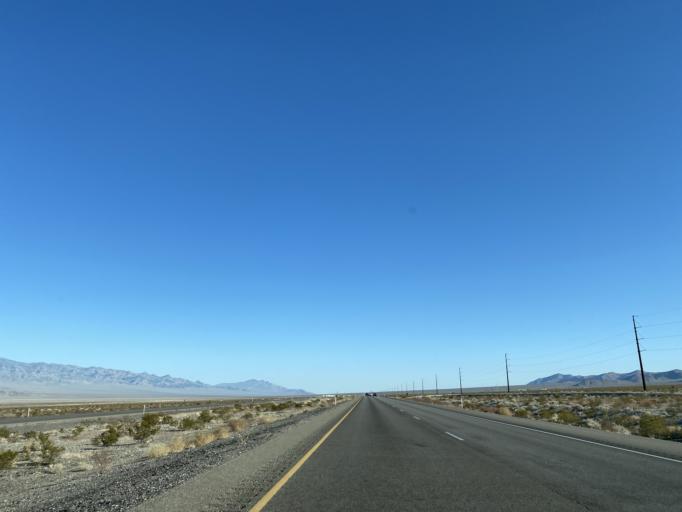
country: US
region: Nevada
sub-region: Clark County
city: Summerlin South
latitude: 36.5455
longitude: -115.5861
